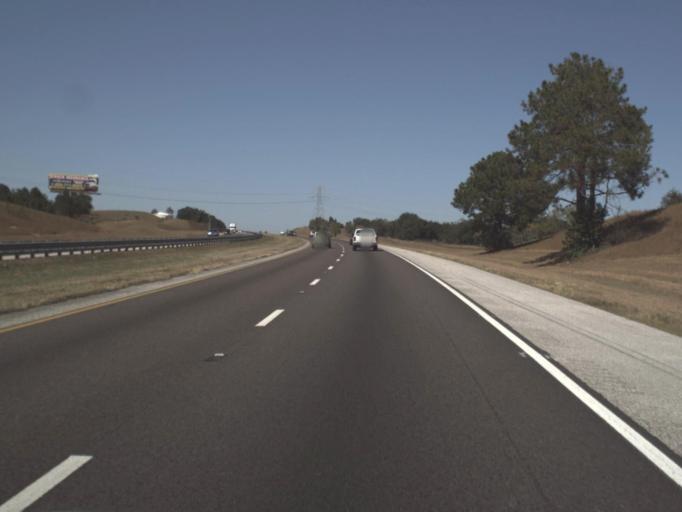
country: US
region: Florida
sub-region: Lake County
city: Minneola
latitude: 28.6101
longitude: -81.7286
